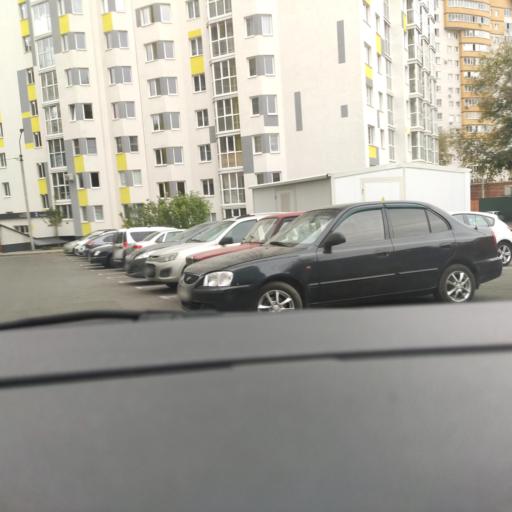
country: RU
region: Voronezj
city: Podgornoye
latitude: 51.6920
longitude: 39.1459
